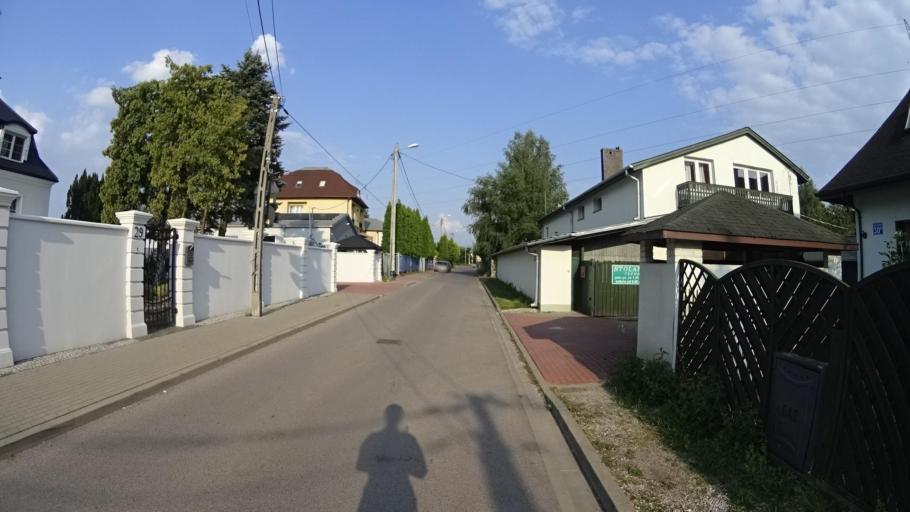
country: PL
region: Masovian Voivodeship
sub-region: Powiat pruszkowski
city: Michalowice
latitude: 52.1758
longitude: 20.8794
